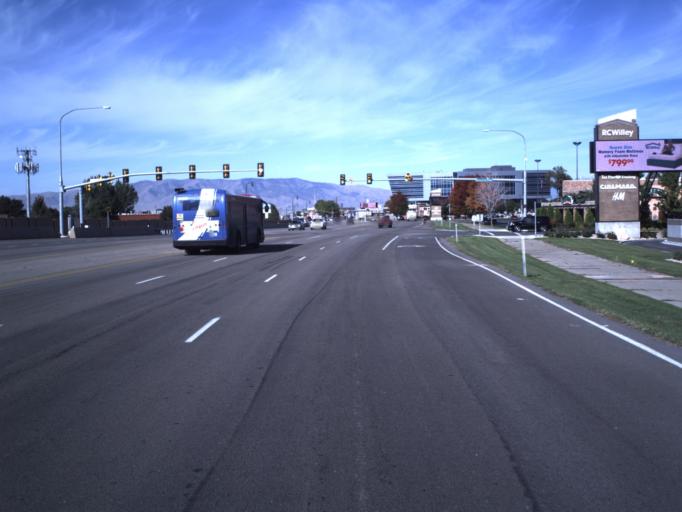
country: US
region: Utah
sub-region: Utah County
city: Orem
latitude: 40.2731
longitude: -111.6778
